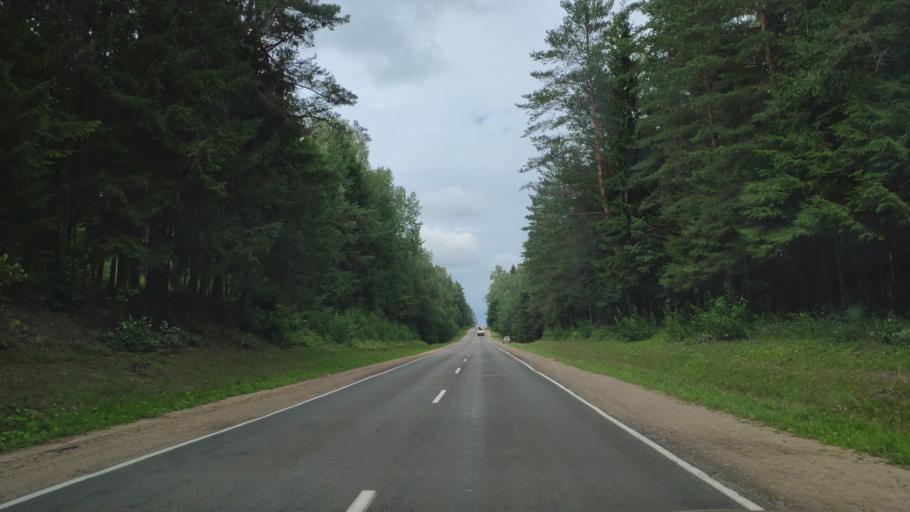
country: BY
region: Minsk
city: Novosel'ye
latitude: 53.9381
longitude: 27.2442
